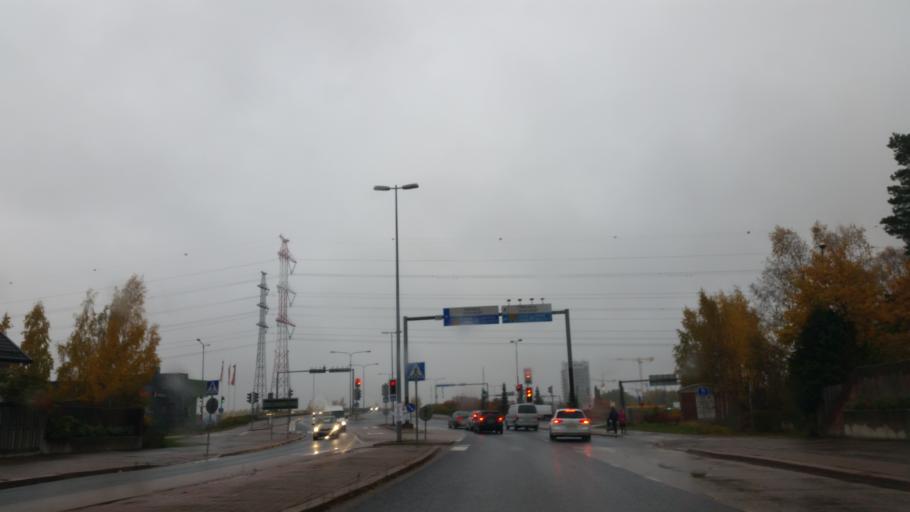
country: FI
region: Uusimaa
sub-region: Helsinki
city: Vantaa
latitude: 60.2807
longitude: 25.0287
